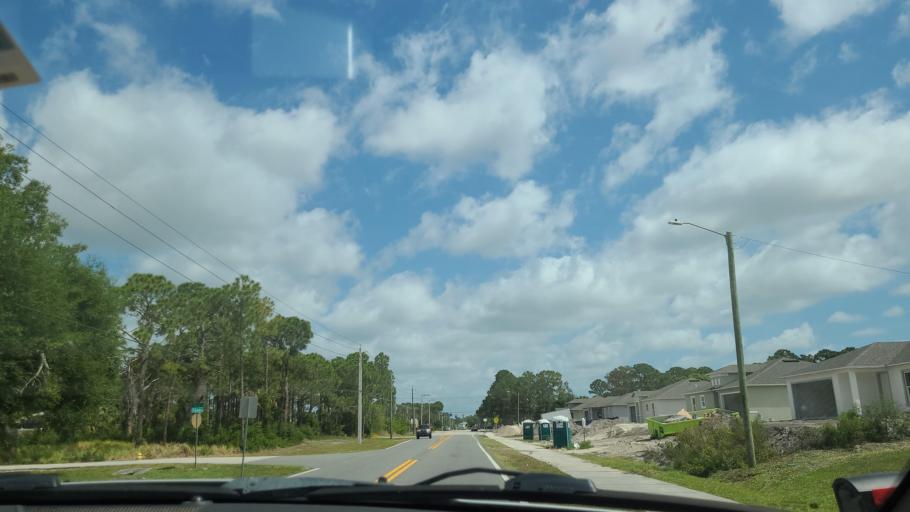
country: US
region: Florida
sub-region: Brevard County
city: West Melbourne
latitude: 27.9850
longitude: -80.6616
